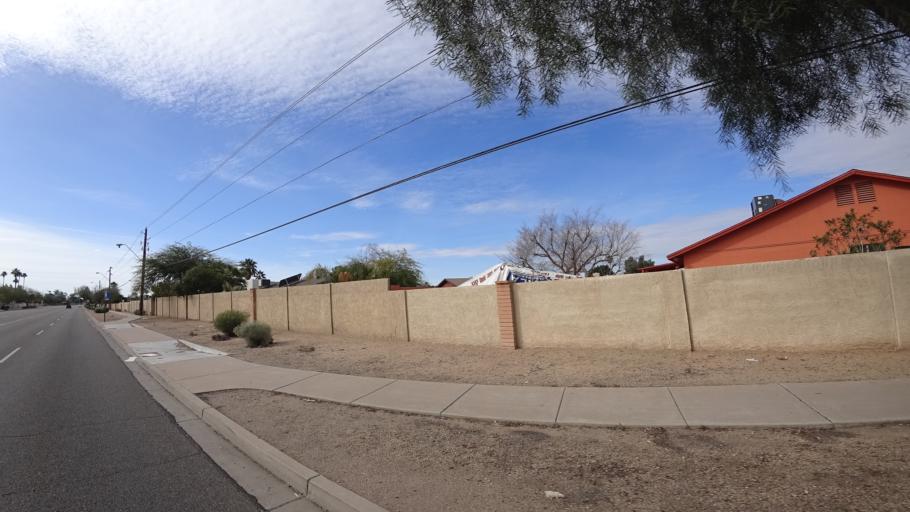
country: US
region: Arizona
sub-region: Maricopa County
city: Peoria
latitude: 33.6361
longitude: -112.1516
